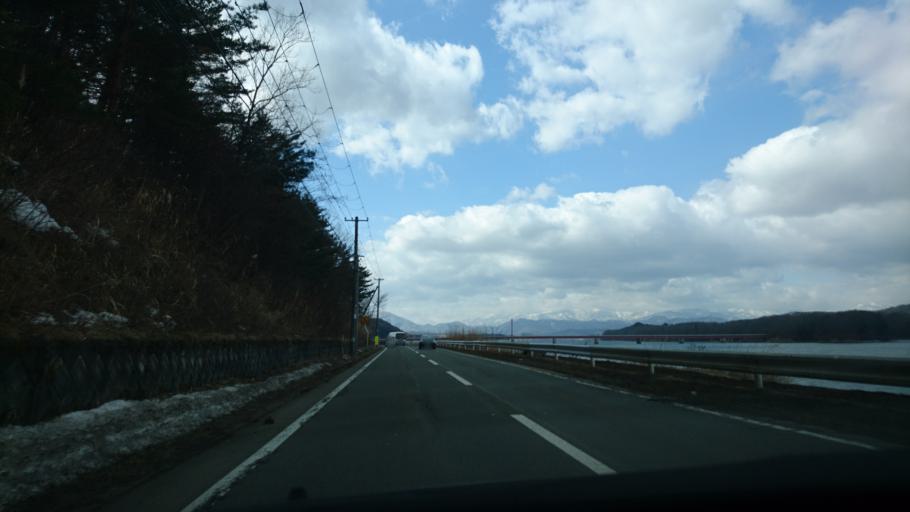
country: JP
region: Iwate
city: Shizukuishi
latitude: 39.6827
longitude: 141.0277
